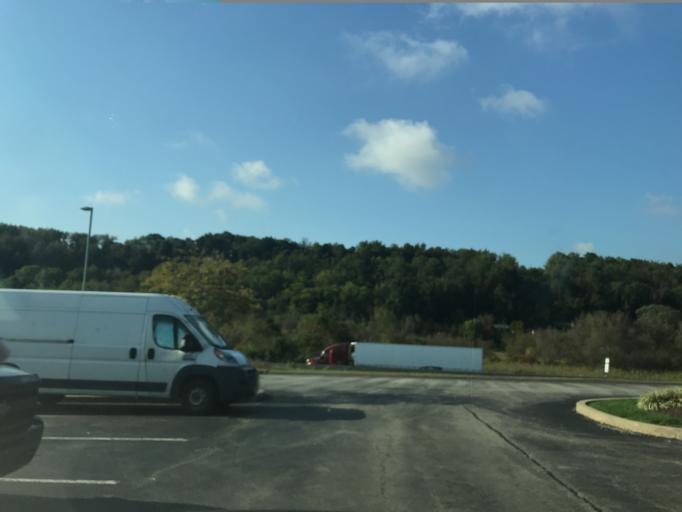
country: US
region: Pennsylvania
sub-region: Westmoreland County
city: Youngwood
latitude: 40.2058
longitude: -79.5658
